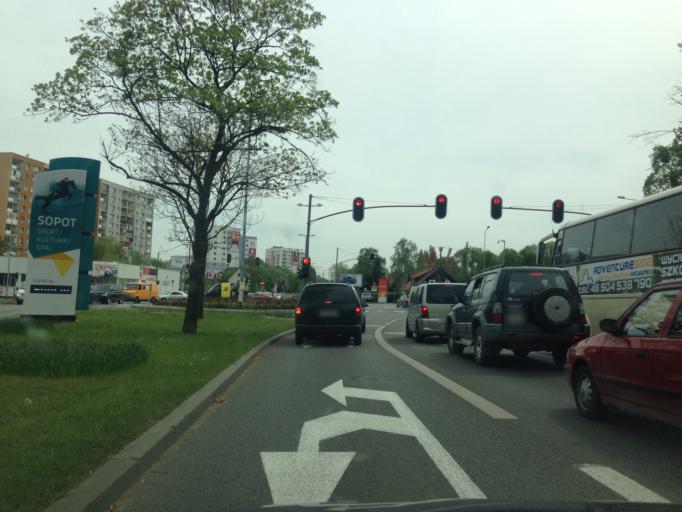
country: PL
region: Pomeranian Voivodeship
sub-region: Sopot
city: Sopot
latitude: 54.4241
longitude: 18.5636
